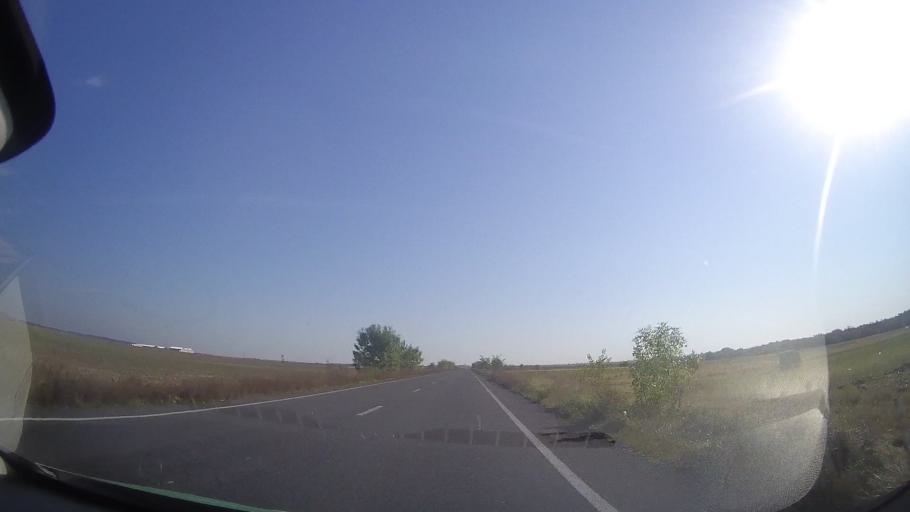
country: RO
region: Timis
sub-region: Comuna Topolovatu Mare
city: Topolovatu Mare
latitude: 45.7752
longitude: 21.6447
